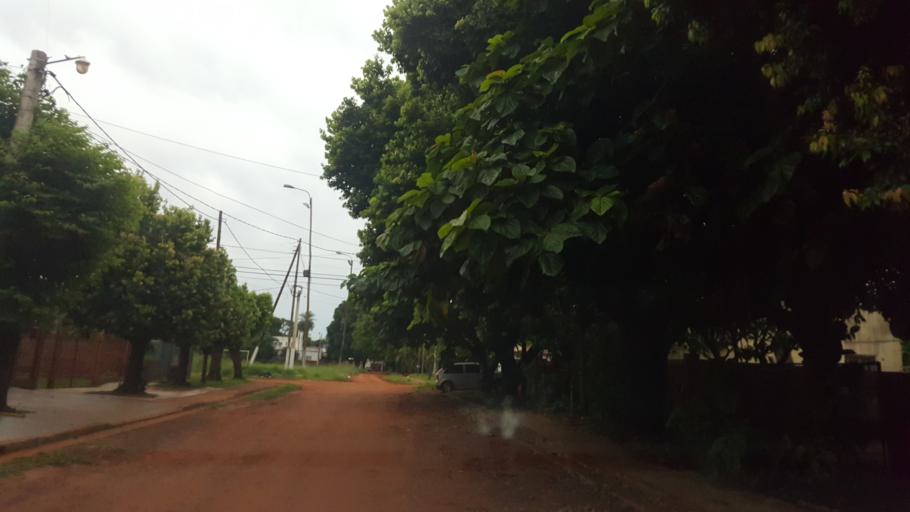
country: AR
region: Misiones
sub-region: Departamento de Capital
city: Posadas
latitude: -27.3692
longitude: -55.9271
